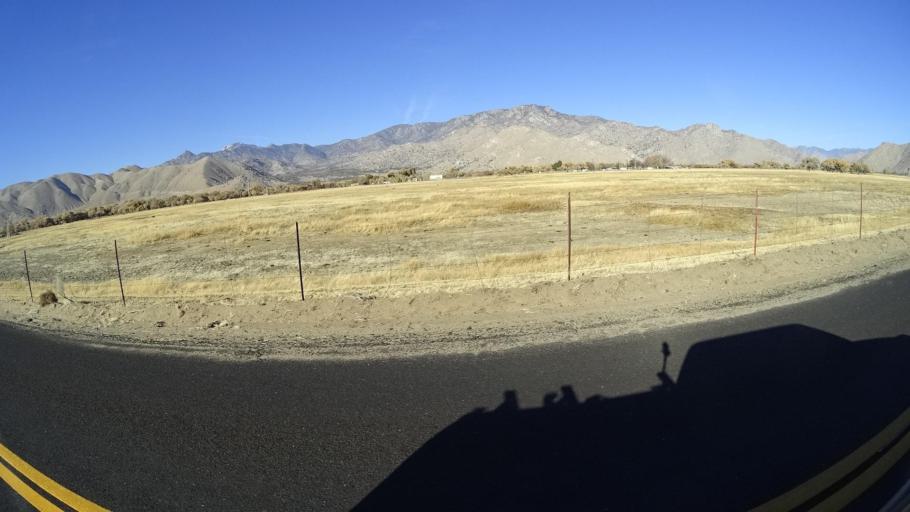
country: US
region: California
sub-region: Kern County
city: Weldon
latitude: 35.6609
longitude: -118.2958
